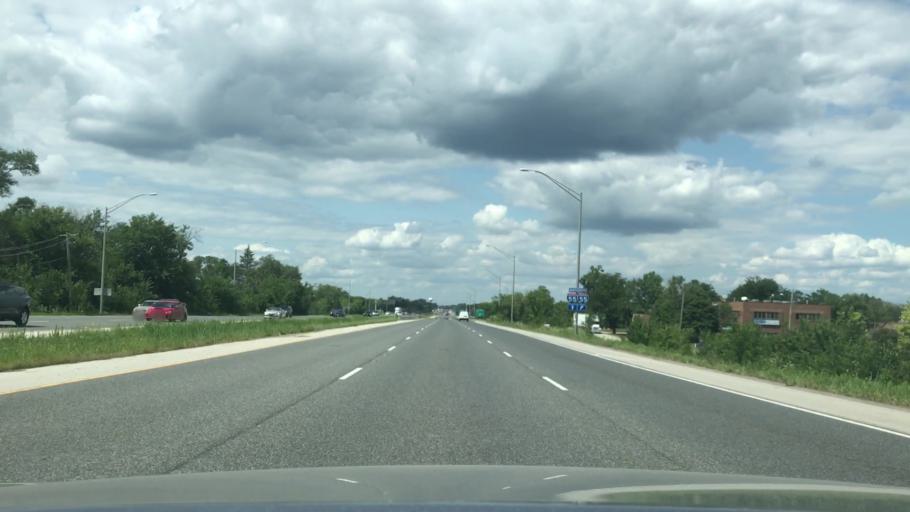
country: US
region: Illinois
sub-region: DuPage County
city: Burr Ridge
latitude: 41.7360
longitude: -87.9441
